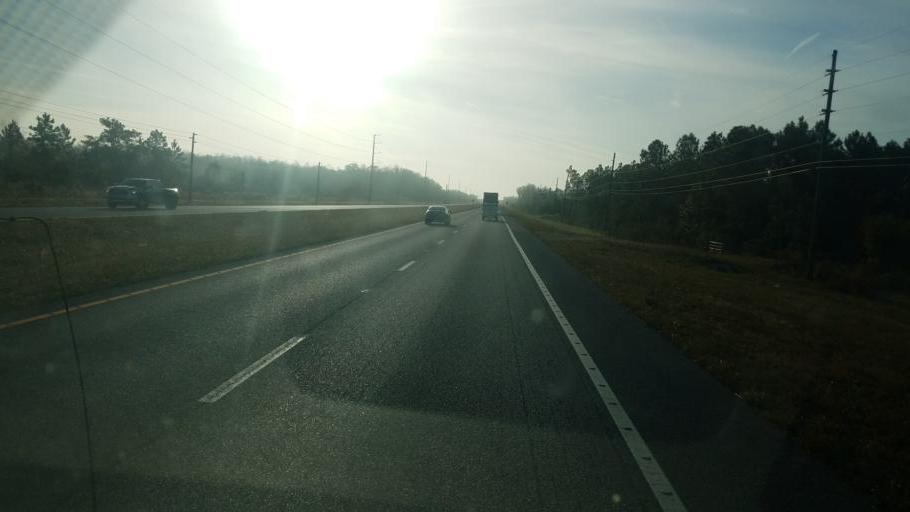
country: US
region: Florida
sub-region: Osceola County
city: Saint Cloud
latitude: 28.1681
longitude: -81.1263
